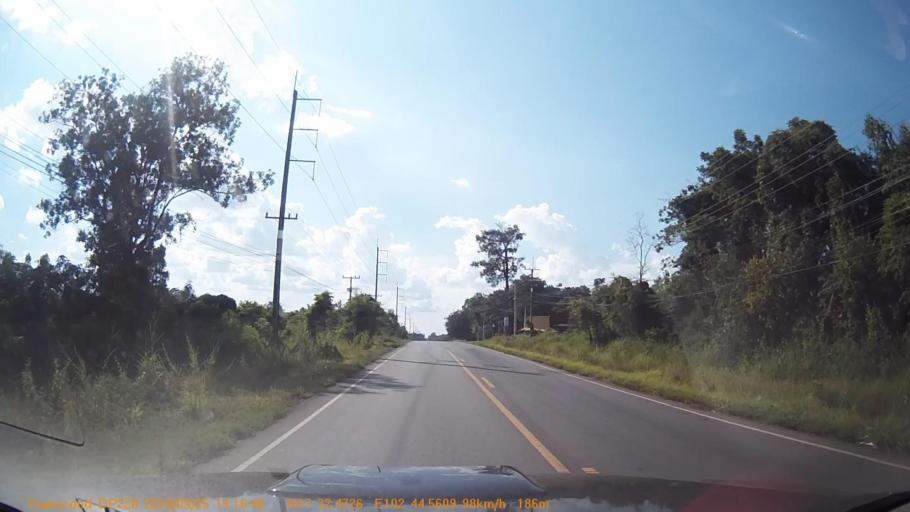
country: TH
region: Changwat Udon Thani
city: Udon Thani
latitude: 17.5414
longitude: 102.7422
